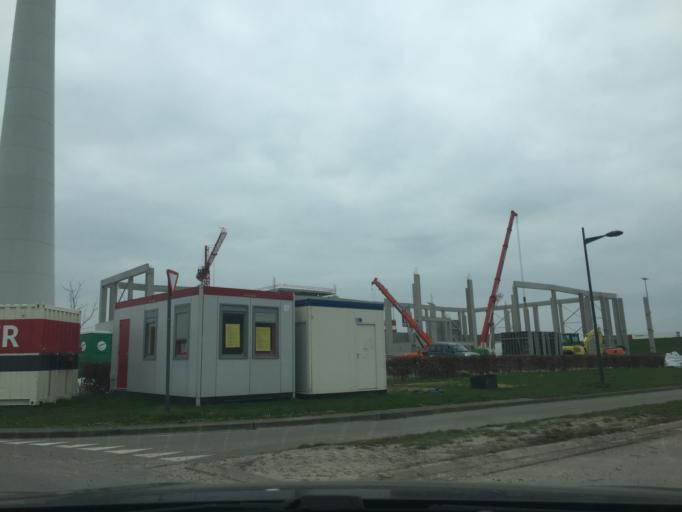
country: BE
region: Flanders
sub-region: Provincie West-Vlaanderen
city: Zwevegem
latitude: 50.8231
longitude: 3.3136
